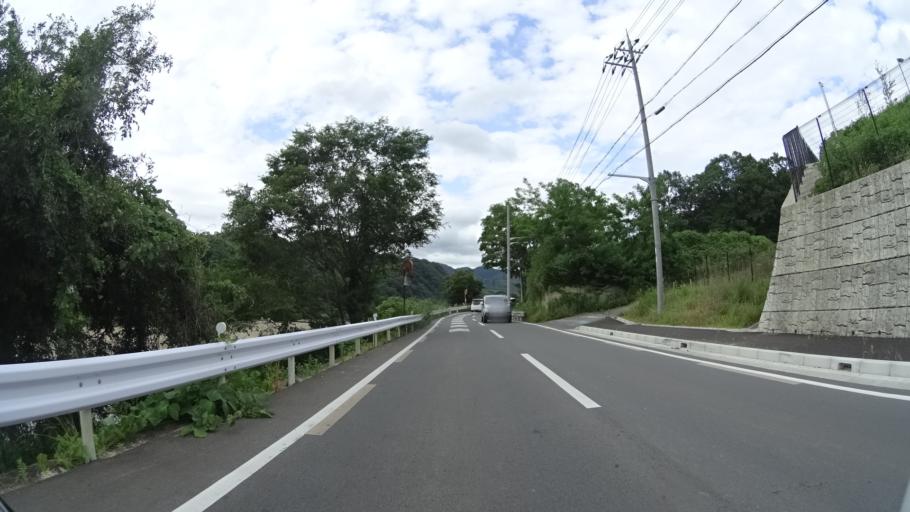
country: JP
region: Nara
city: Nara-shi
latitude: 34.7536
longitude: 135.8403
